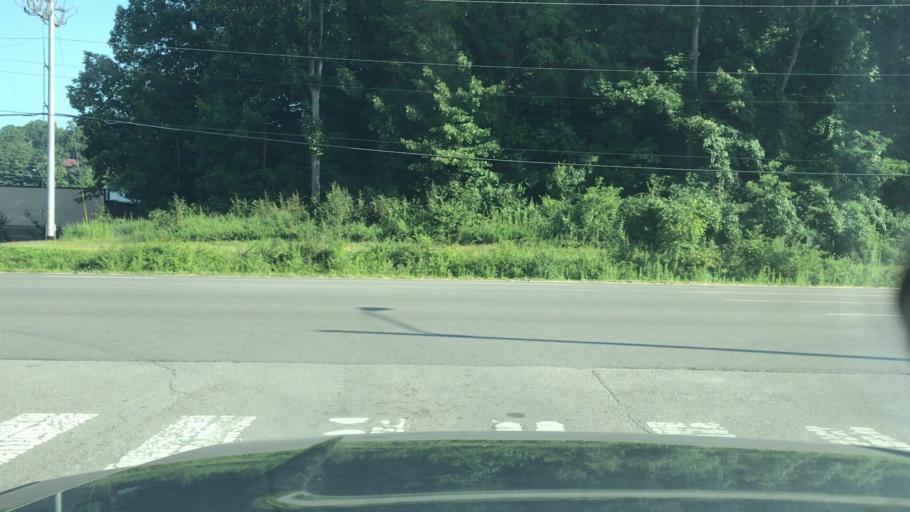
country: US
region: Tennessee
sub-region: Davidson County
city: Belle Meade
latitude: 36.0750
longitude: -86.9186
